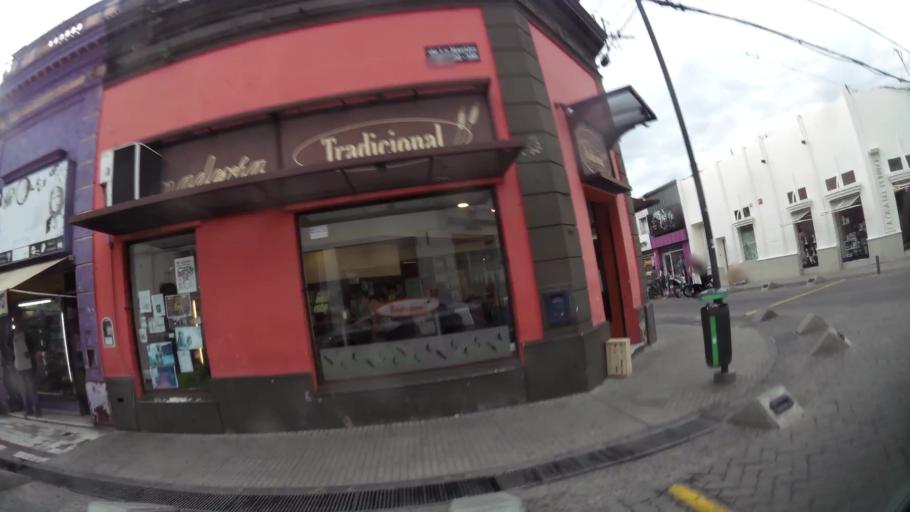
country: AR
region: Buenos Aires
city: San Nicolas de los Arroyos
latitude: -33.3343
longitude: -60.2205
